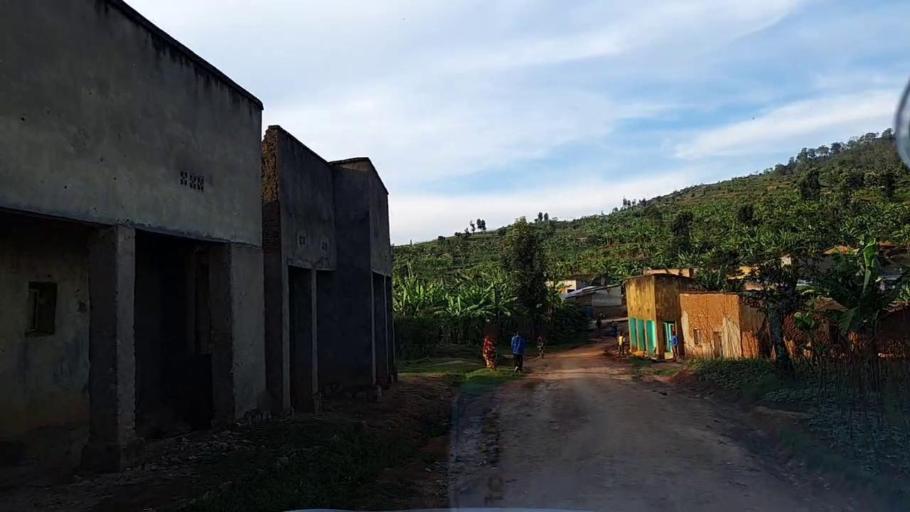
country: RW
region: Southern Province
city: Gikongoro
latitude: -2.3975
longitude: 29.5541
